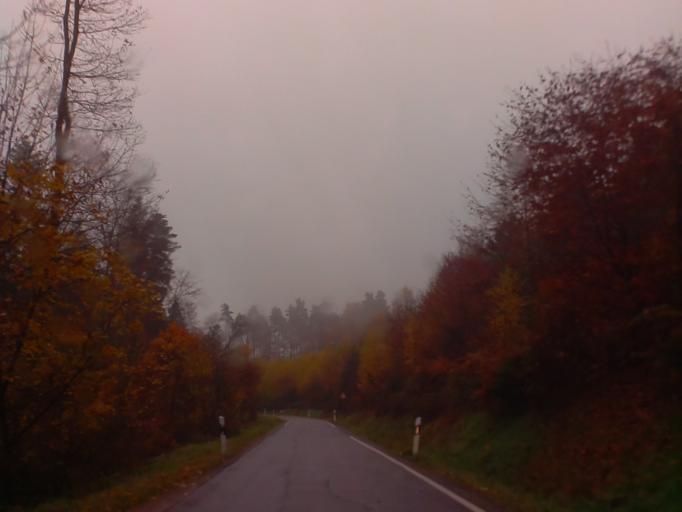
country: DE
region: Hesse
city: Neckarsteinach
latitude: 49.4258
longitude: 8.8514
